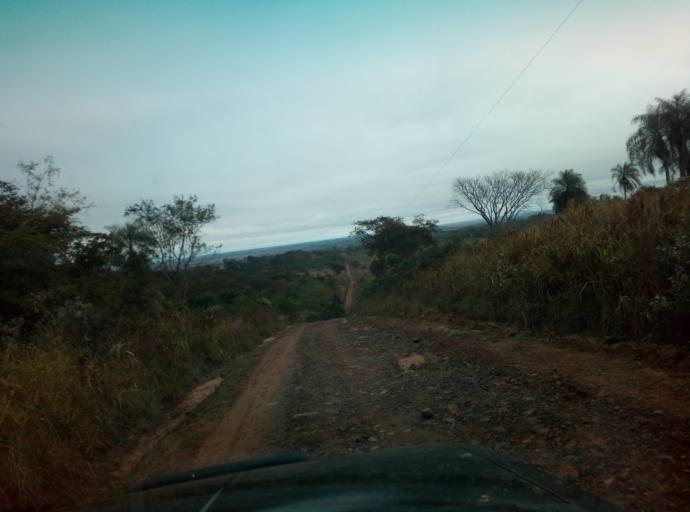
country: PY
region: Caaguazu
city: Carayao
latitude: -25.1904
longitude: -56.3670
